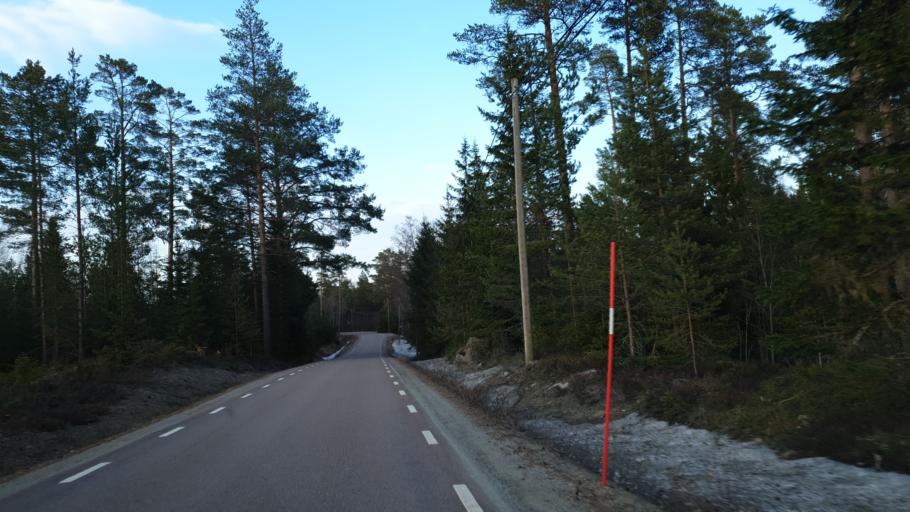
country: SE
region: Vaesternorrland
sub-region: Sundsvalls Kommun
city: Njurundabommen
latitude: 62.2375
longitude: 17.5202
